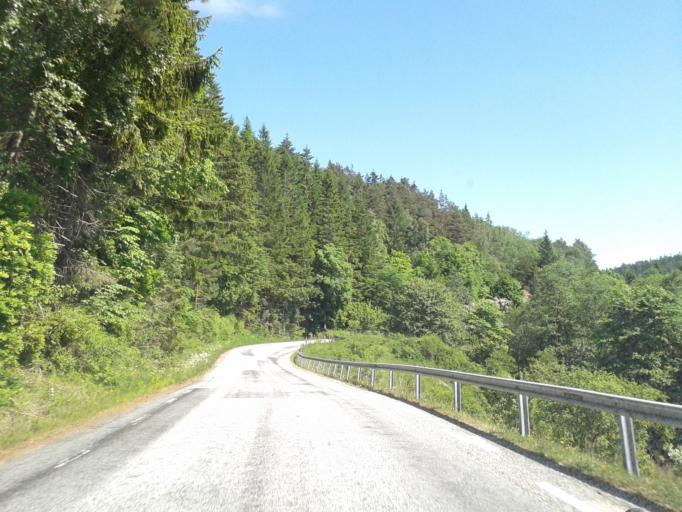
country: SE
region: Vaestra Goetaland
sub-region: Stenungsunds Kommun
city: Stora Hoga
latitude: 58.0190
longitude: 11.8901
